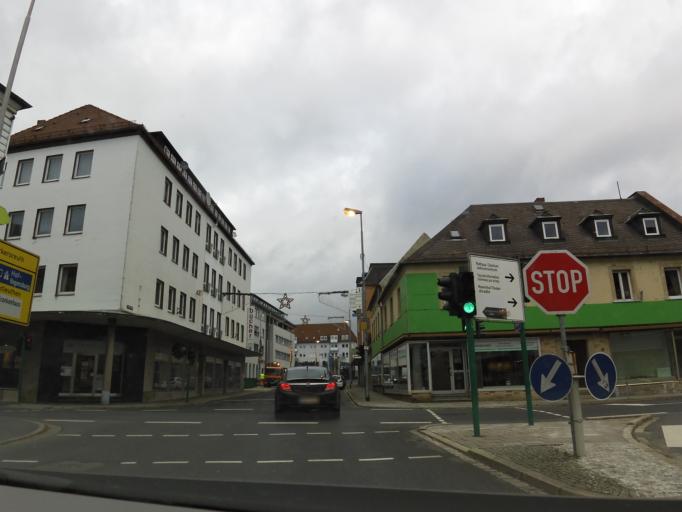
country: DE
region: Bavaria
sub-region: Upper Franconia
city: Selb
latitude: 50.1698
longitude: 12.1279
